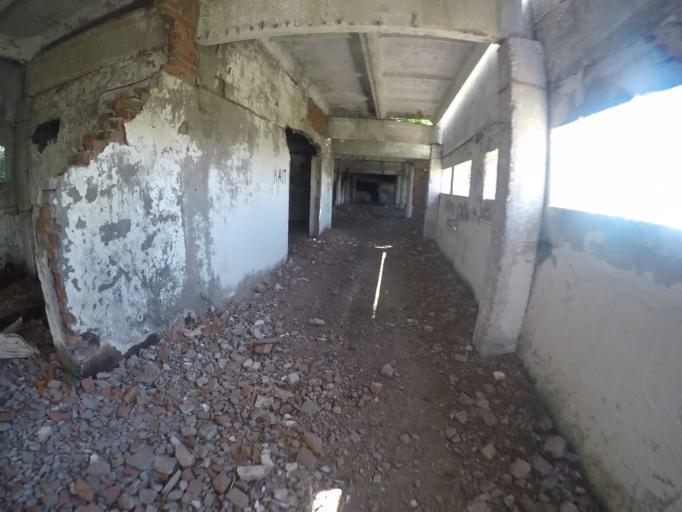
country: RU
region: Saratov
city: Krasnoarmeysk
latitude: 51.1686
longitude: 45.9105
